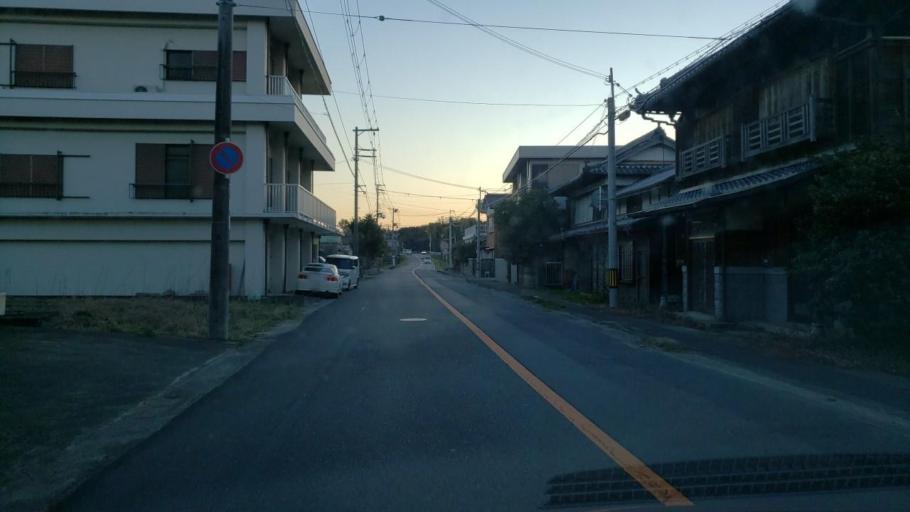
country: JP
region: Hyogo
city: Fukura
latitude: 34.3286
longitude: 134.7739
